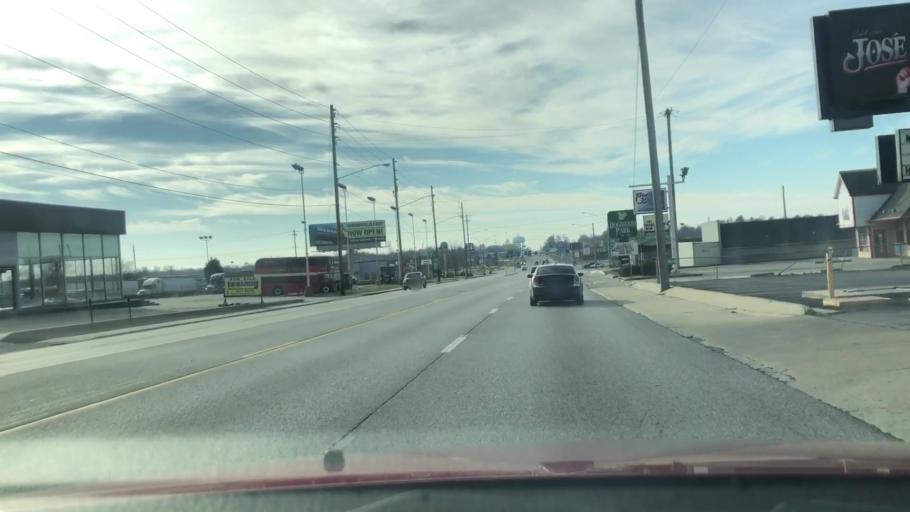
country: US
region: Missouri
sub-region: Greene County
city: Springfield
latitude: 37.2172
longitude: -93.2617
